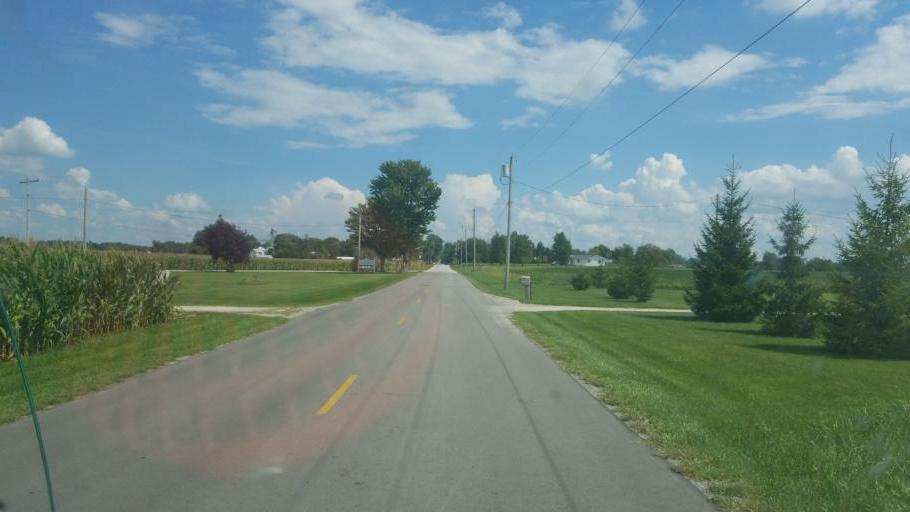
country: US
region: Ohio
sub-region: Hardin County
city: Forest
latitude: 40.8613
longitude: -83.4724
